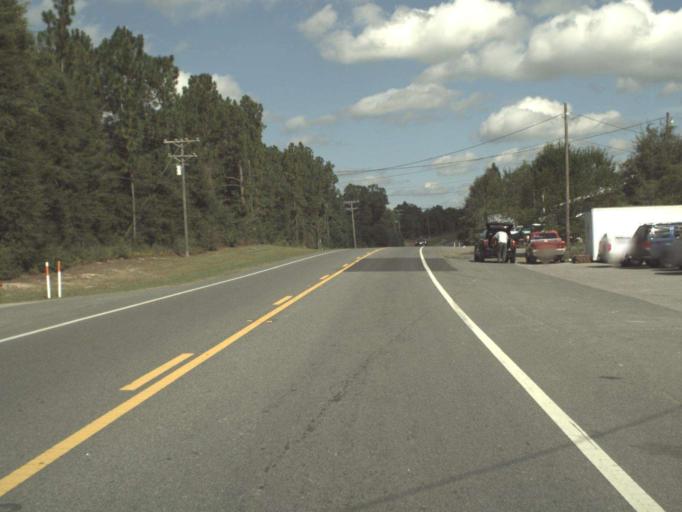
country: US
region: Florida
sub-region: Walton County
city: DeFuniak Springs
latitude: 30.7374
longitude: -86.1153
